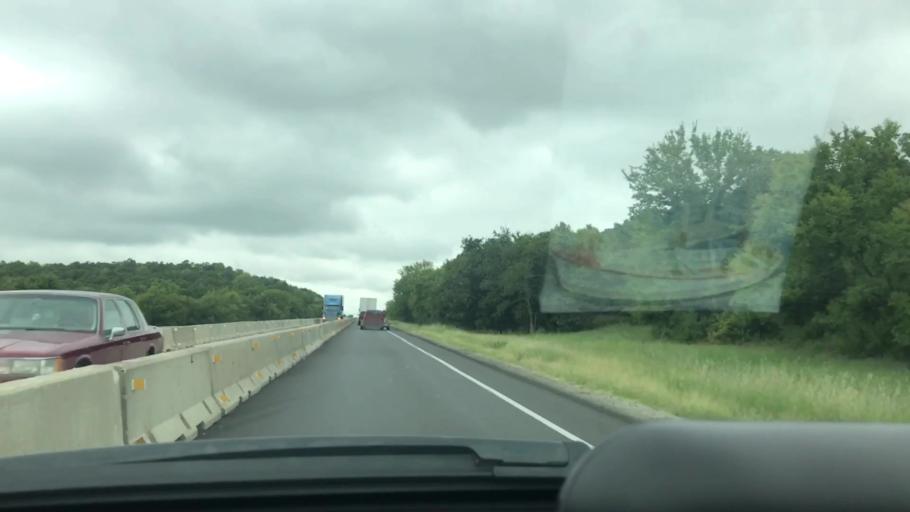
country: US
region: Oklahoma
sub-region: McIntosh County
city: Eufaula
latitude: 35.2674
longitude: -95.5908
